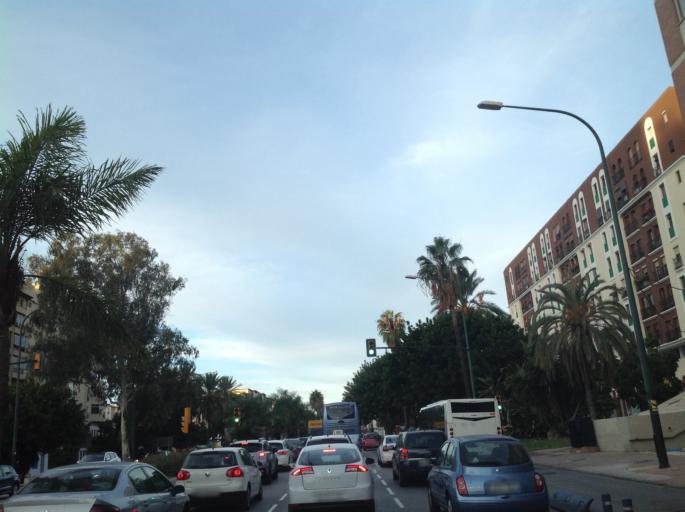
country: ES
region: Andalusia
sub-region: Provincia de Malaga
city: Malaga
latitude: 36.7167
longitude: -4.4399
